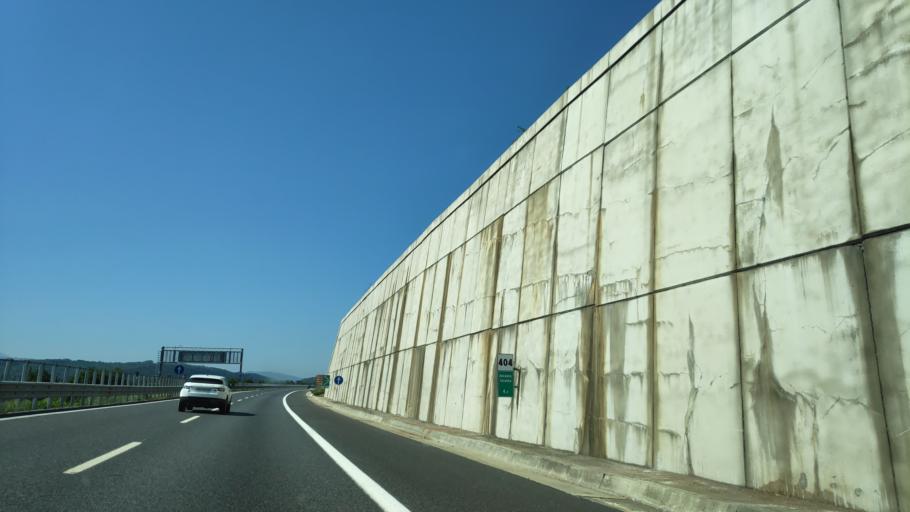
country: IT
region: Calabria
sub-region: Provincia di Reggio Calabria
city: Seminara
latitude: 38.3494
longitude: 15.8705
